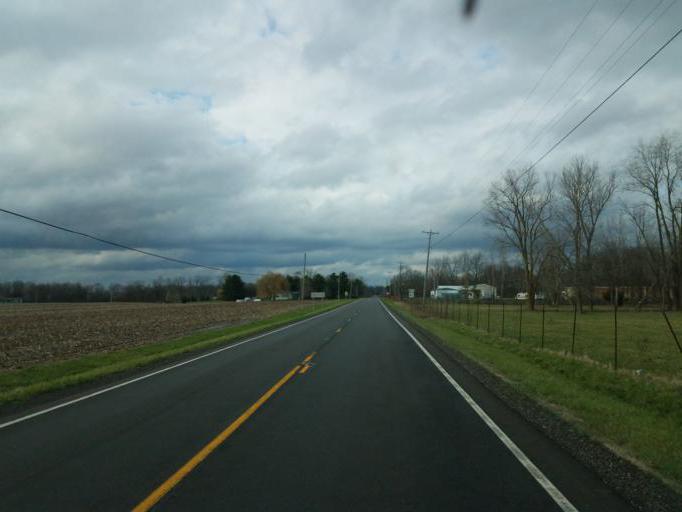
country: US
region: Ohio
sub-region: Delaware County
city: Ashley
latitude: 40.4543
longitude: -82.9509
